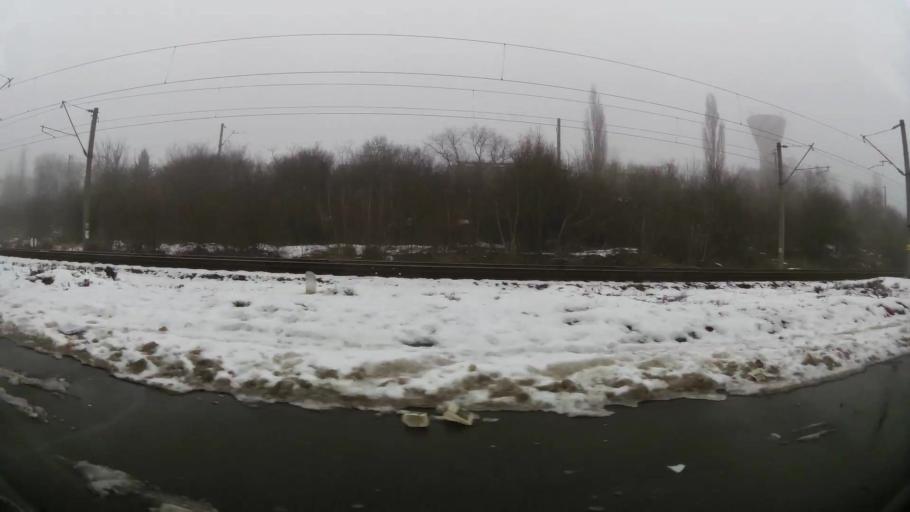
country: RO
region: Ilfov
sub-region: Comuna Chiajna
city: Rosu
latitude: 44.4701
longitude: 26.0347
